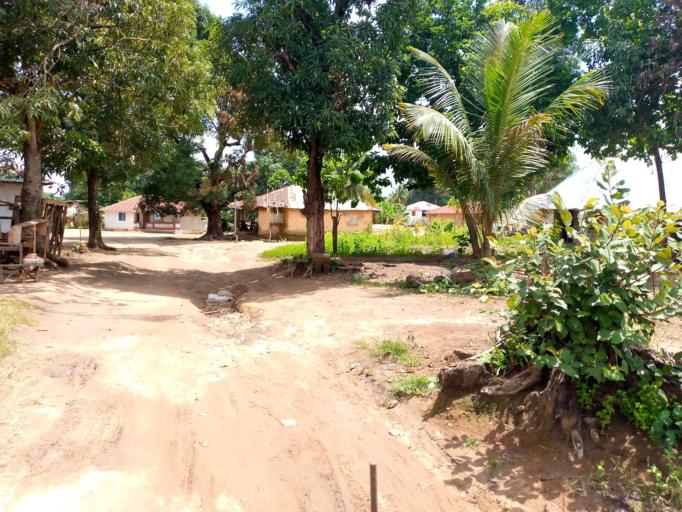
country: SL
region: Northern Province
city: Magburaka
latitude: 8.7309
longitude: -11.9433
